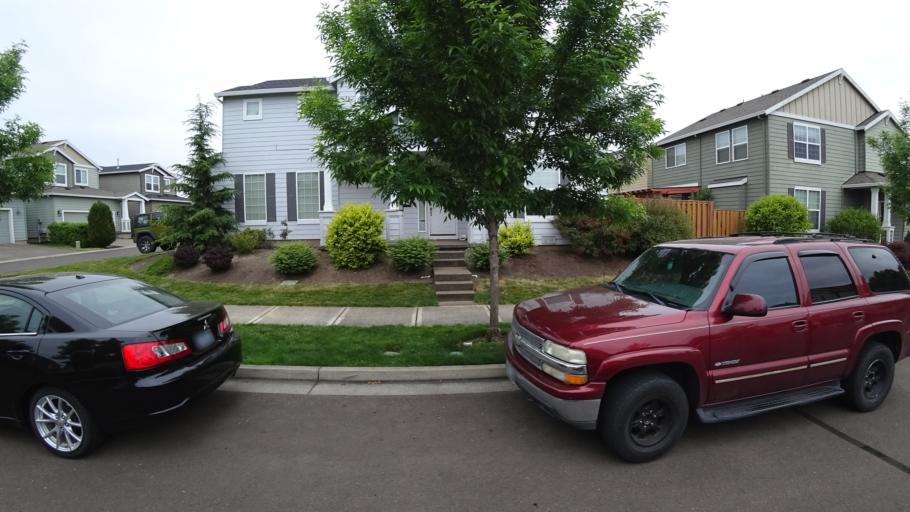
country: US
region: Oregon
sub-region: Washington County
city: Aloha
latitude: 45.4955
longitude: -122.9207
